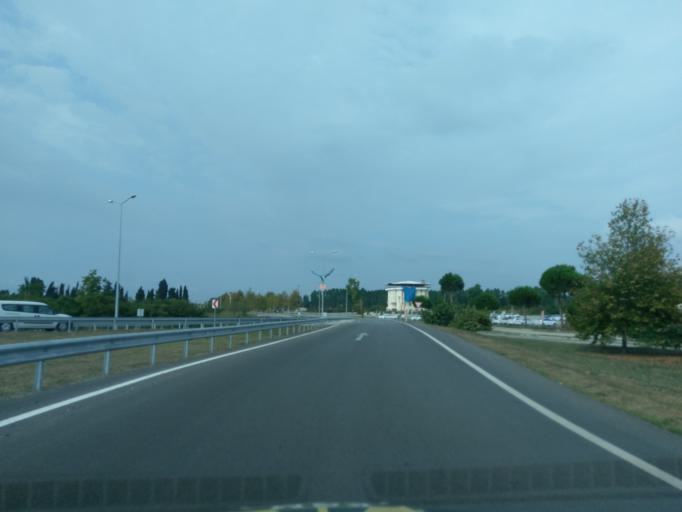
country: TR
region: Samsun
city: Dikbiyik
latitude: 41.2378
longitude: 36.5391
